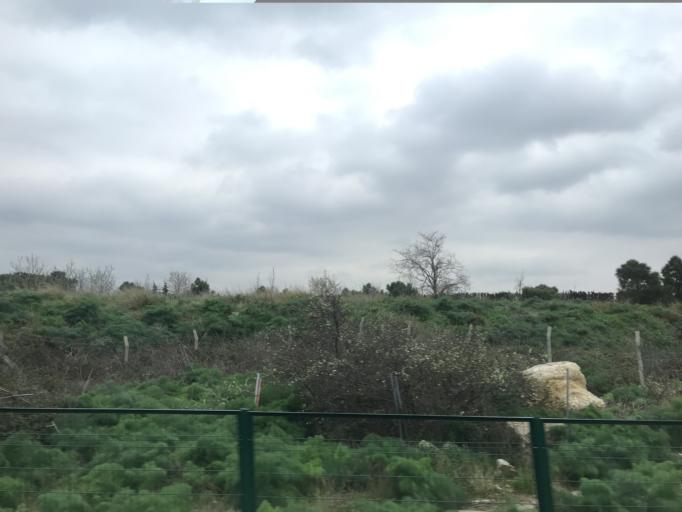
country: TR
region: Istanbul
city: Bahcelievler
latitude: 40.9642
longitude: 28.8073
